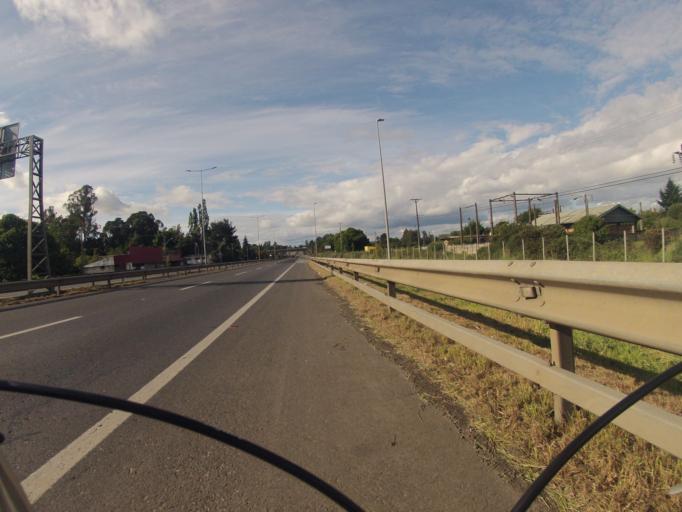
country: CL
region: Araucania
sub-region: Provincia de Cautin
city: Temuco
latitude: -38.8303
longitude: -72.6238
